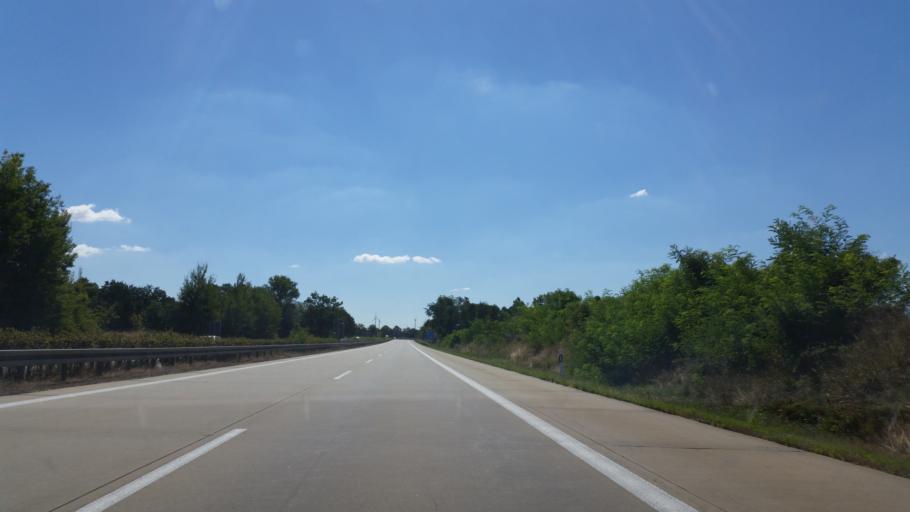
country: DE
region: Brandenburg
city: Vetschau
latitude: 51.7967
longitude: 14.0504
